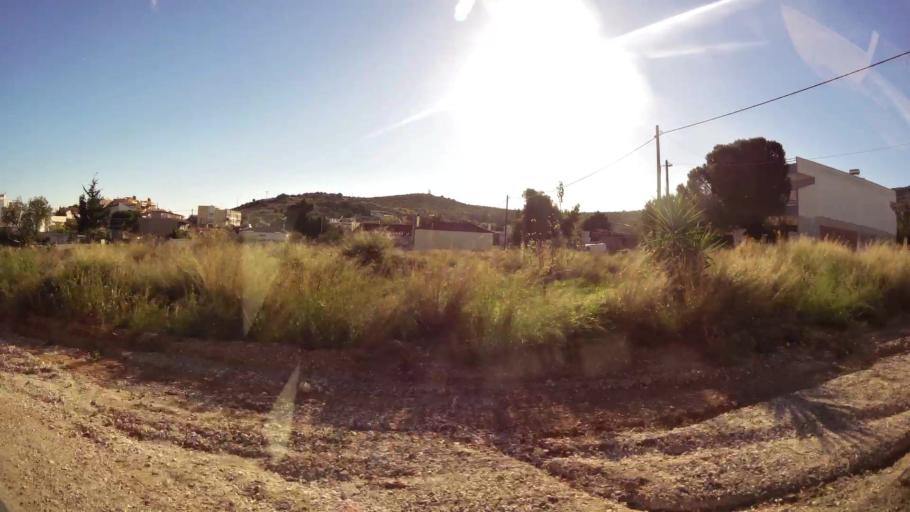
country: GR
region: Attica
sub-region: Nomarchia Anatolikis Attikis
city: Koropi
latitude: 37.8954
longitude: 23.8632
